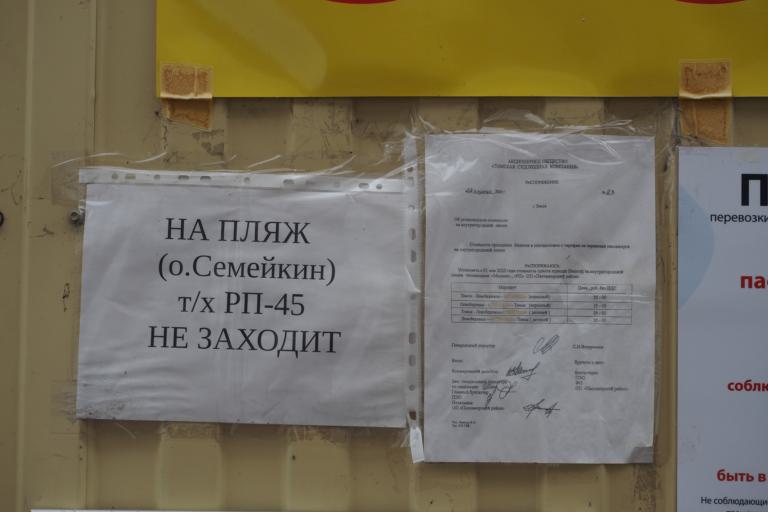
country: RU
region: Tomsk
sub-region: Tomskiy Rayon
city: Tomsk
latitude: 56.4939
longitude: 84.9424
